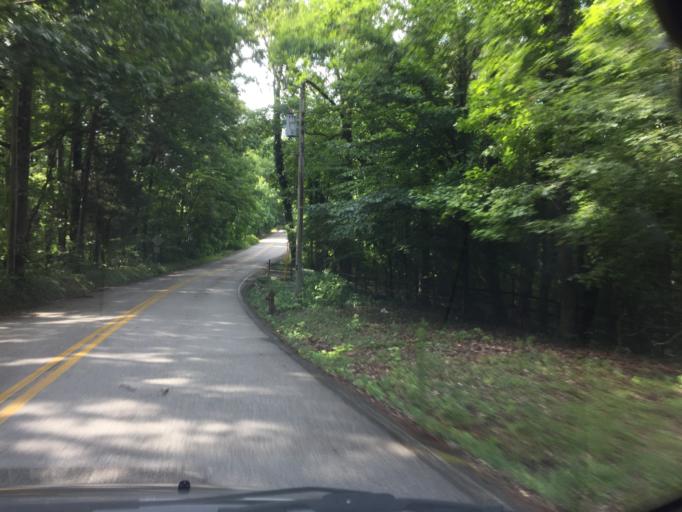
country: US
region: Tennessee
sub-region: Hamilton County
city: Apison
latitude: 35.0120
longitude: -85.0528
